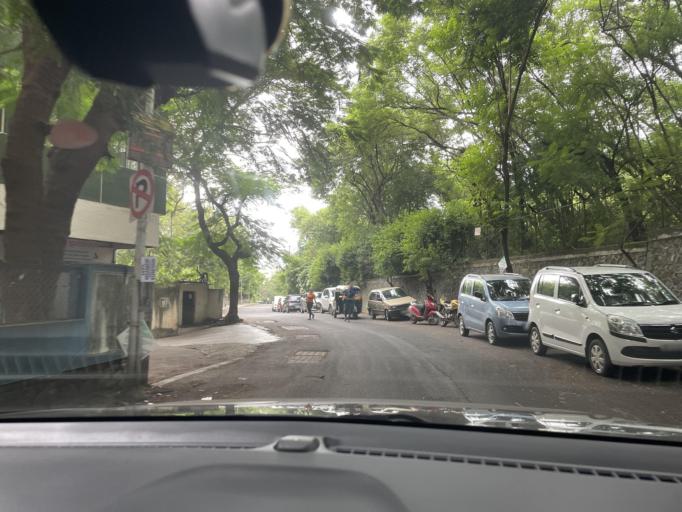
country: IN
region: Maharashtra
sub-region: Pune Division
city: Shivaji Nagar
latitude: 18.5323
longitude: 73.8138
